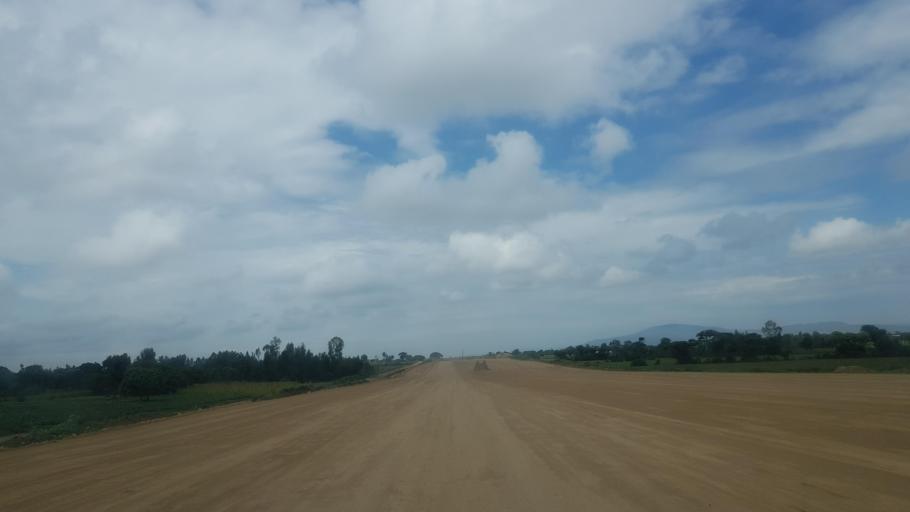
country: ET
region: Oromiya
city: Shashemene
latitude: 7.2422
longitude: 38.5824
